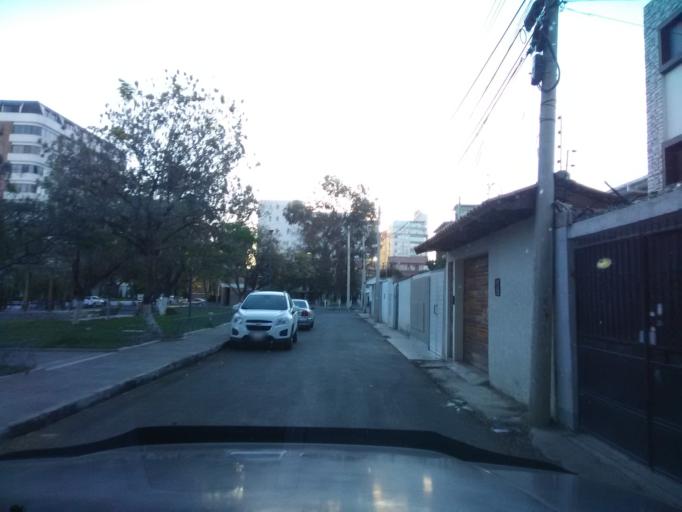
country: BO
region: Cochabamba
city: Cochabamba
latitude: -17.3753
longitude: -66.1476
